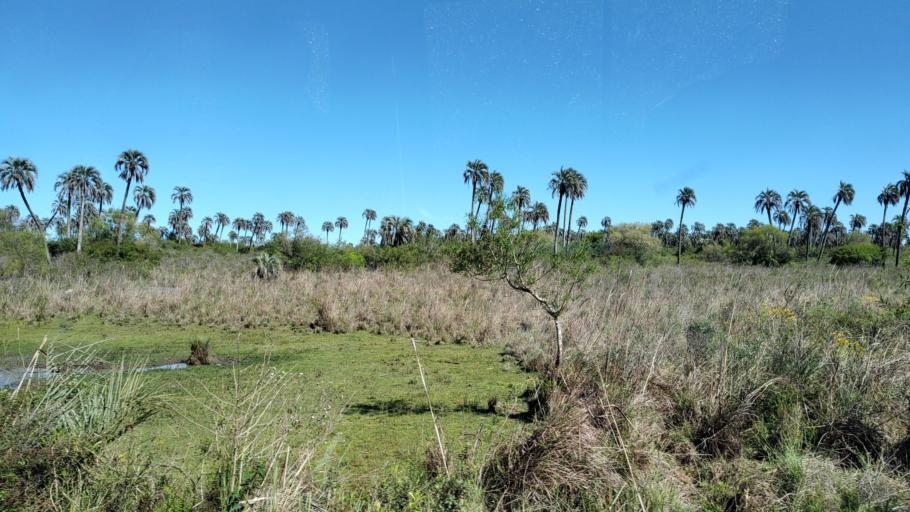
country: AR
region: Entre Rios
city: Ubajay
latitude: -31.8887
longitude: -58.2415
